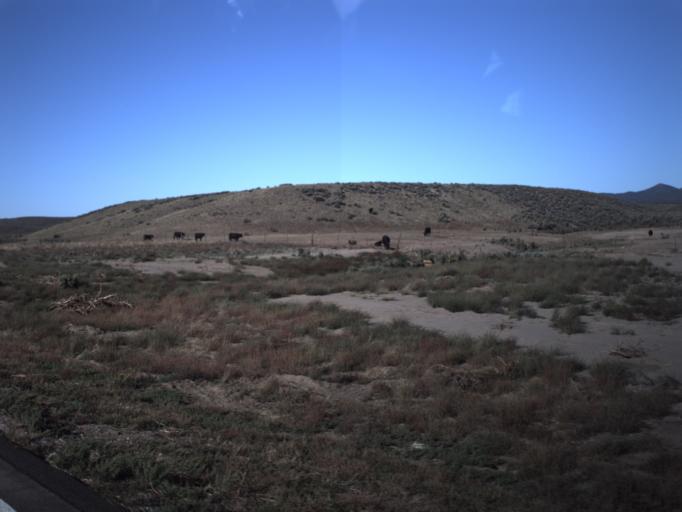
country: US
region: Utah
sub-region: Washington County
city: Enterprise
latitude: 37.7805
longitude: -113.9667
